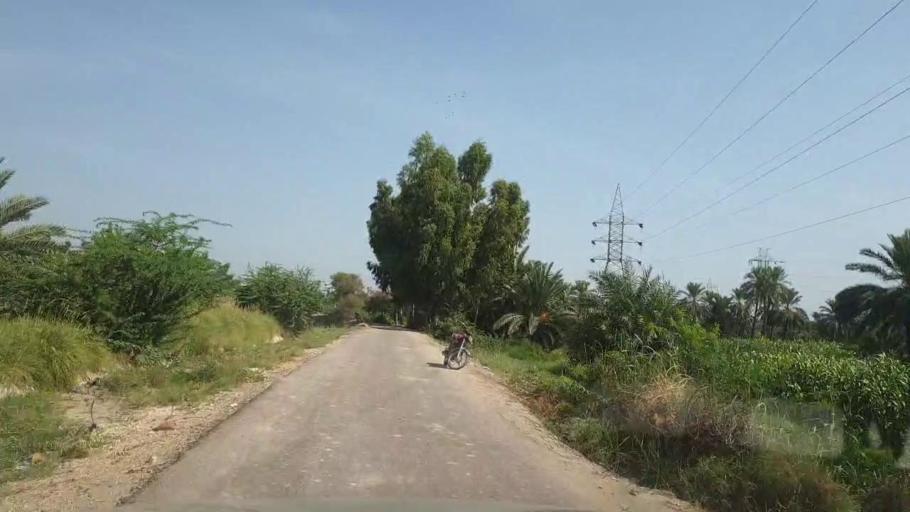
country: PK
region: Sindh
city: Rohri
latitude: 27.6700
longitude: 68.8822
